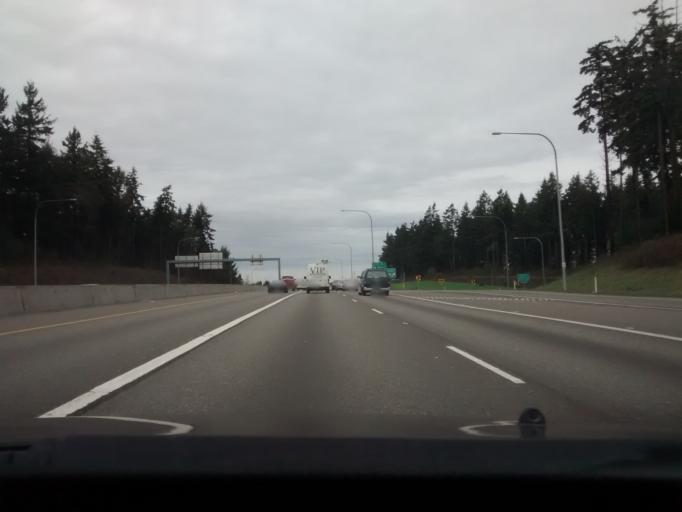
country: US
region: Washington
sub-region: Pierce County
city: Fircrest
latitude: 47.2445
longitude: -122.5059
